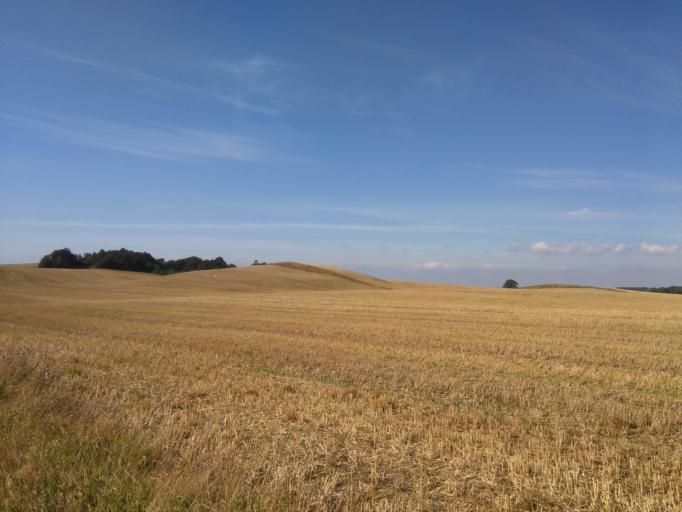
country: DK
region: Central Jutland
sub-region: Syddjurs Kommune
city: Ebeltoft
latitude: 56.2429
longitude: 10.7626
